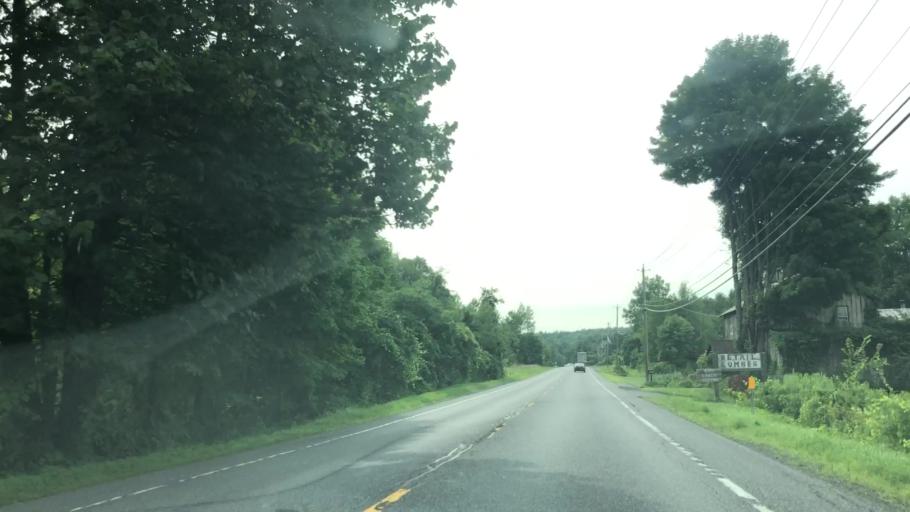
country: US
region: New York
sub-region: Warren County
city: Queensbury
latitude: 43.4037
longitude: -73.5907
